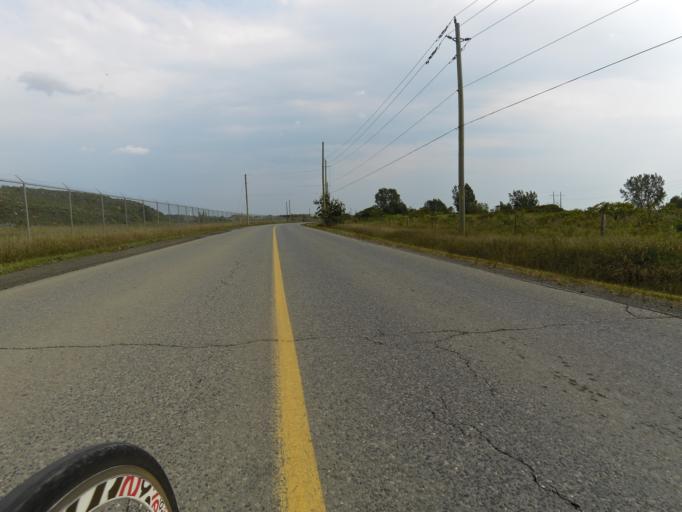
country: CA
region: Ontario
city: Bells Corners
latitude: 45.2349
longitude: -75.7800
